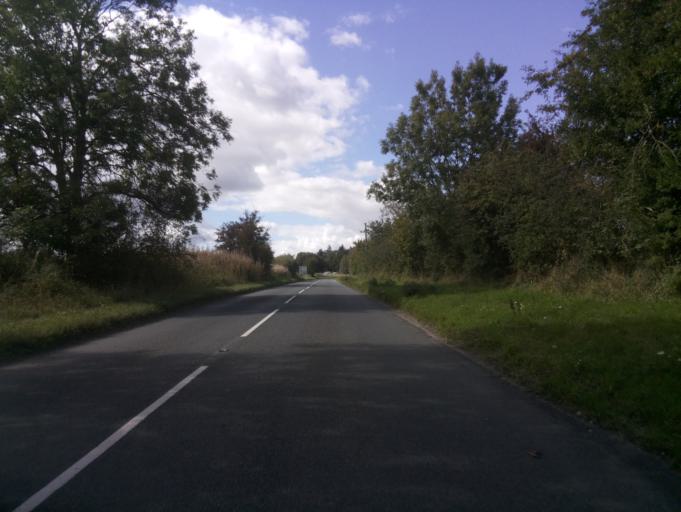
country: GB
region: England
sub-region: Wiltshire
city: Erlestoke
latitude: 51.2811
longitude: -2.0307
